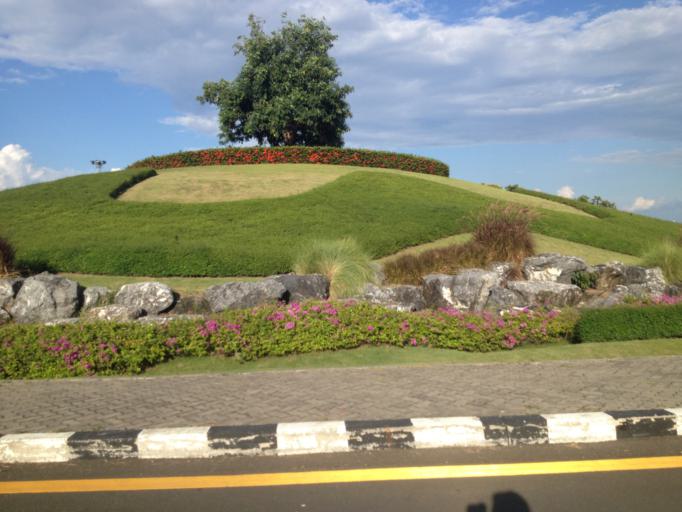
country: TH
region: Chiang Mai
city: Hang Dong
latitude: 18.7469
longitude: 98.9250
